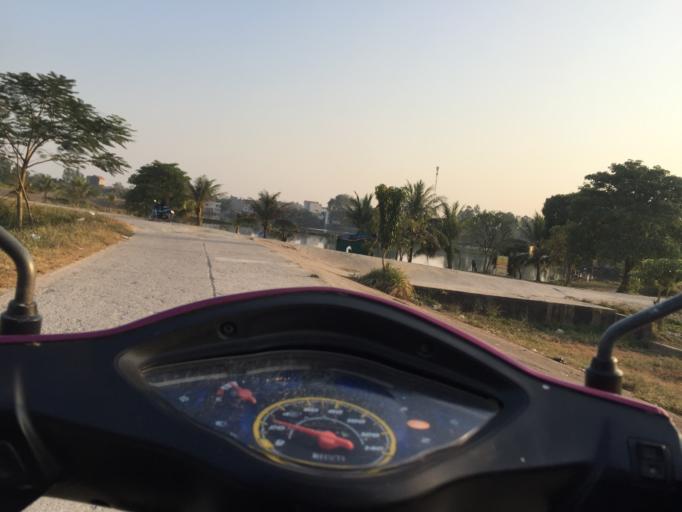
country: VN
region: Ha Noi
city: Chuc Son
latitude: 20.9077
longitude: 105.7146
